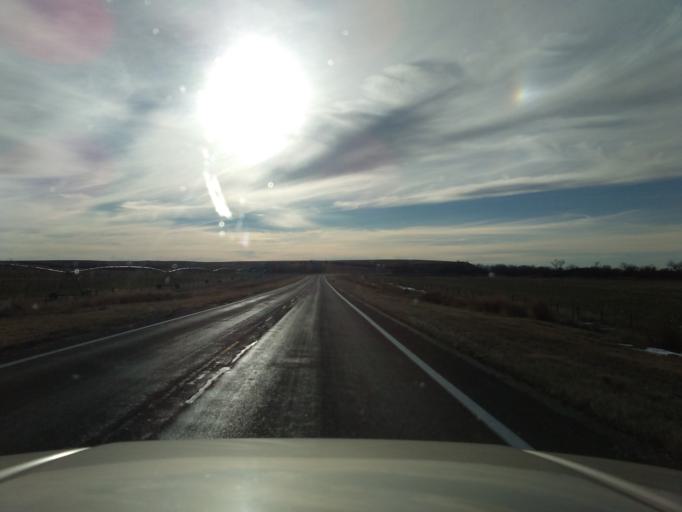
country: US
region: Kansas
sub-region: Norton County
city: Norton
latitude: 39.7262
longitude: -100.1862
